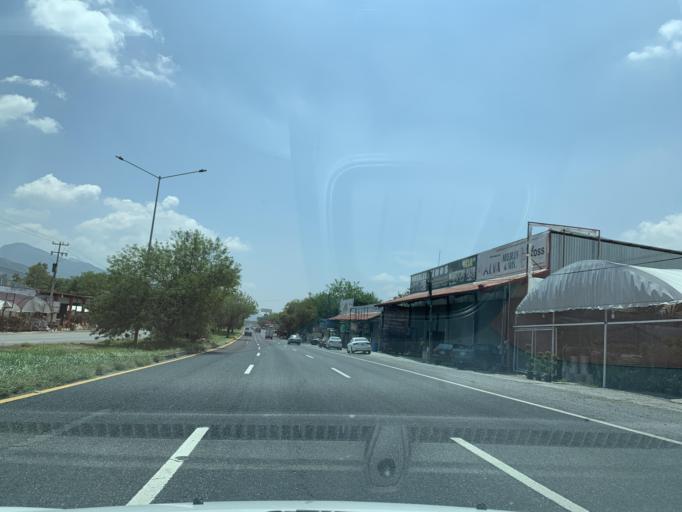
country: MX
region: Nuevo Leon
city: Santiago
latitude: 25.4596
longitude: -100.1694
